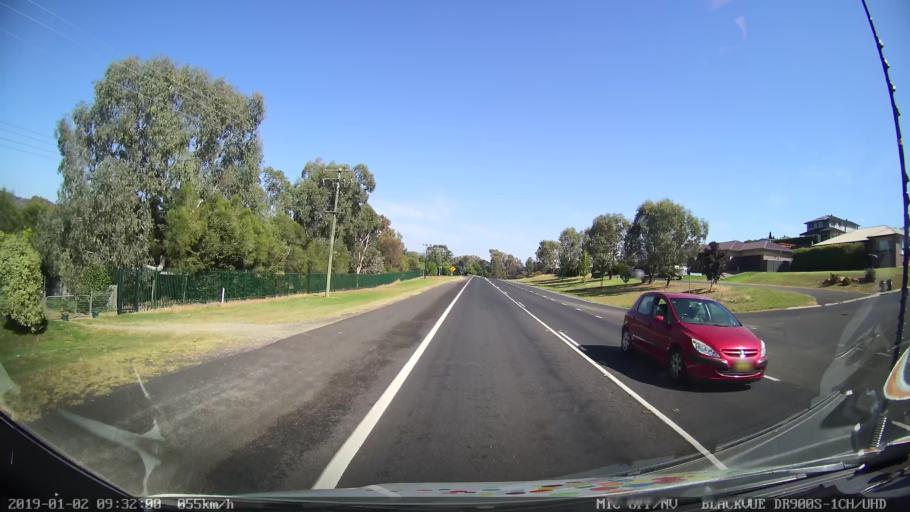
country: AU
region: New South Wales
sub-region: Tumut Shire
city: Tumut
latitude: -35.3148
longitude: 148.2322
